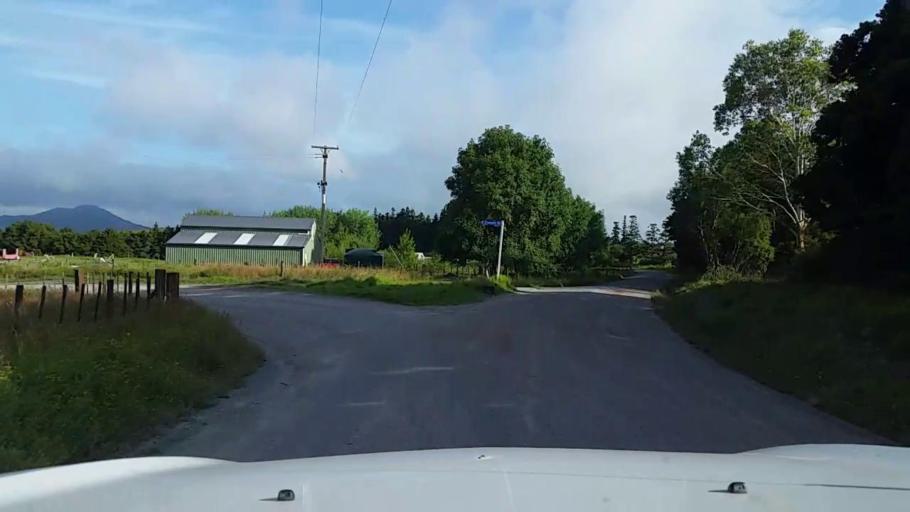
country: NZ
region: Northland
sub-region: Whangarei
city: Maungatapere
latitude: -35.6802
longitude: 174.1784
